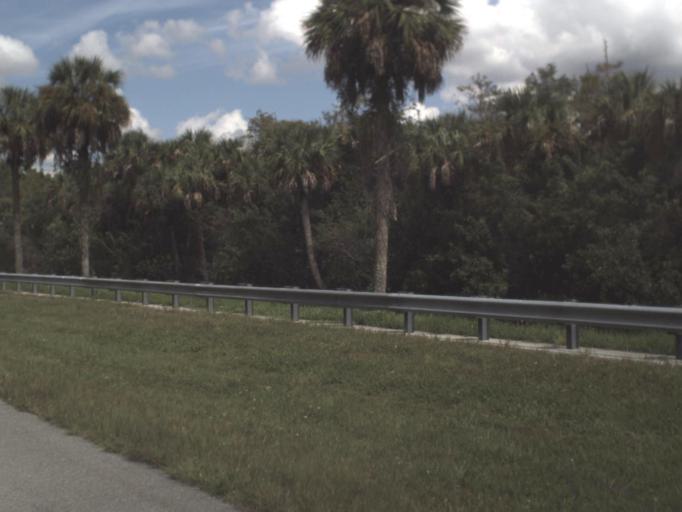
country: US
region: Florida
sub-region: Collier County
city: Lely Resort
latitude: 25.9920
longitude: -81.3474
